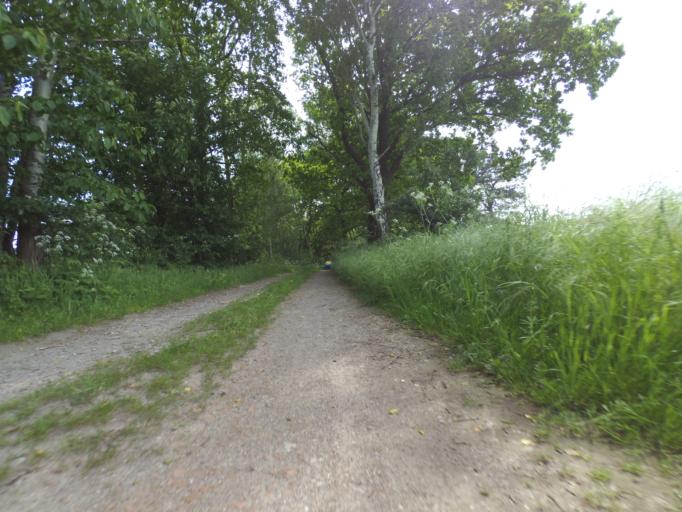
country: DE
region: Lower Saxony
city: Arpke
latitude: 52.3519
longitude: 10.1384
